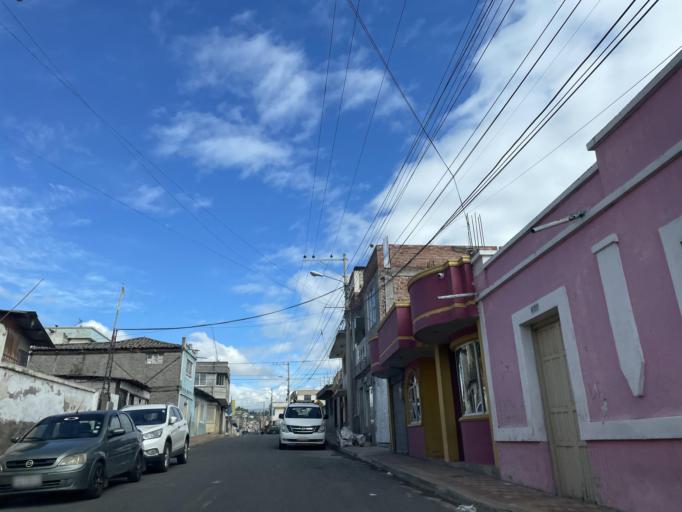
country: EC
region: Chimborazo
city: Guano
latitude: -1.6080
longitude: -78.6305
